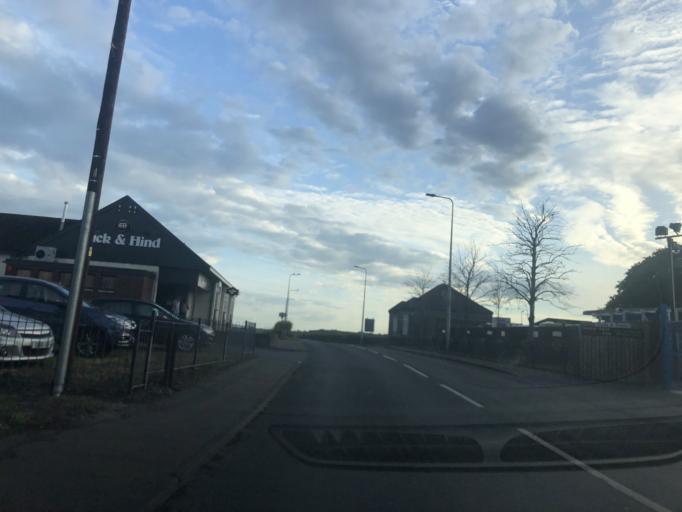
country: GB
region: Scotland
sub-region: Fife
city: Buckhaven
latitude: 56.1737
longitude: -3.0416
